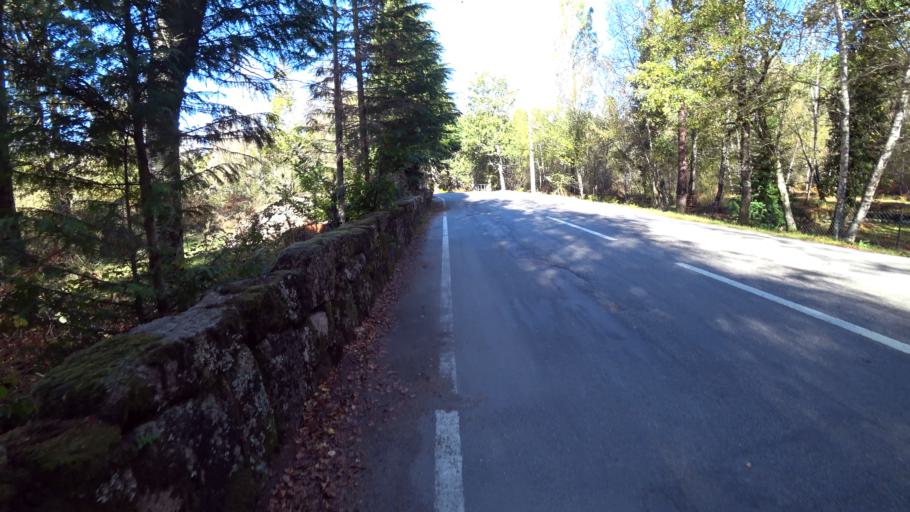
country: PT
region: Braga
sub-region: Vieira do Minho
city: Real
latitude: 41.7552
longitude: -8.1933
